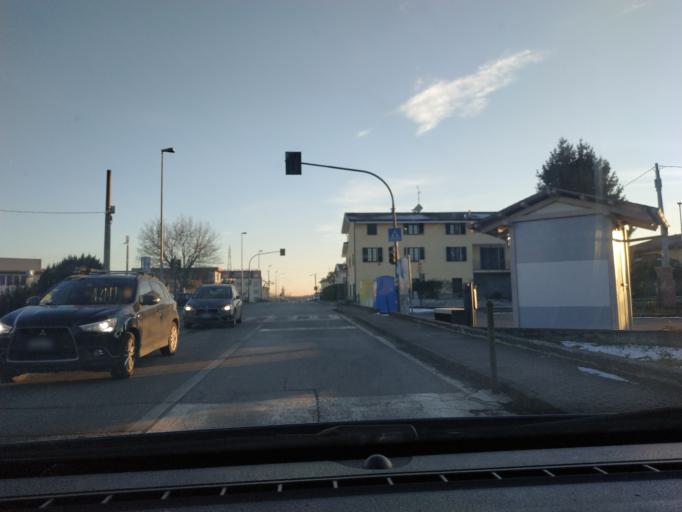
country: IT
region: Piedmont
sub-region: Provincia di Torino
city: Romano Canavese
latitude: 45.4257
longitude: 7.8826
